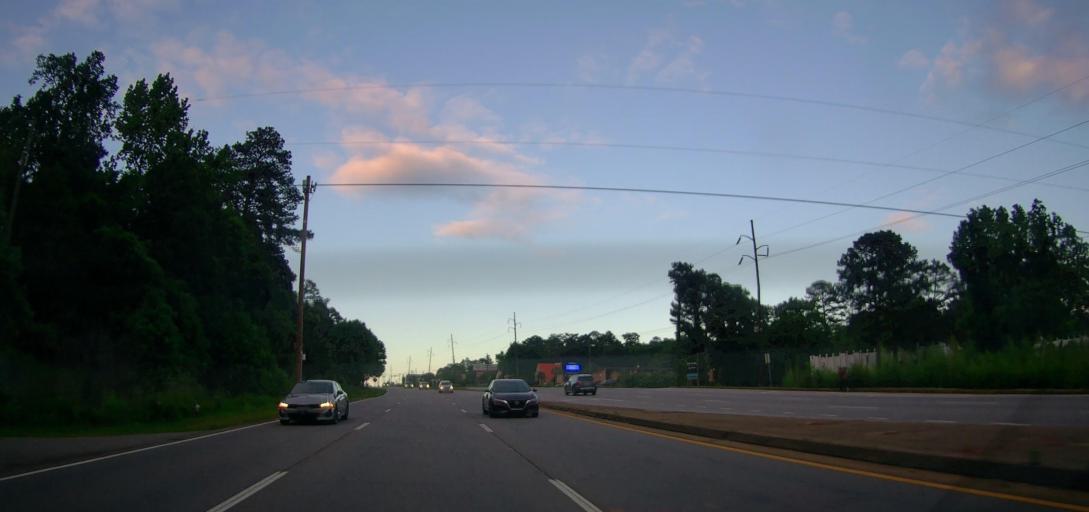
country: US
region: Georgia
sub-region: Clarke County
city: Country Club Estates
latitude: 33.9471
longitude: -83.4216
